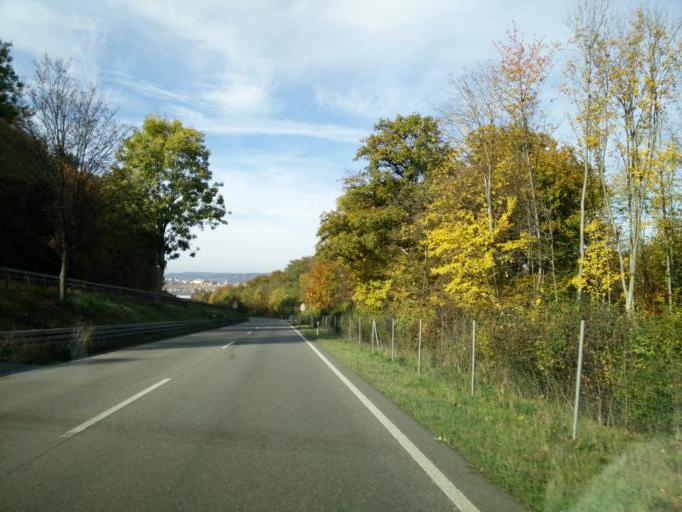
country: DE
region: Baden-Wuerttemberg
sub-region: Tuebingen Region
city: Kusterdingen
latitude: 48.5099
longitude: 9.0950
